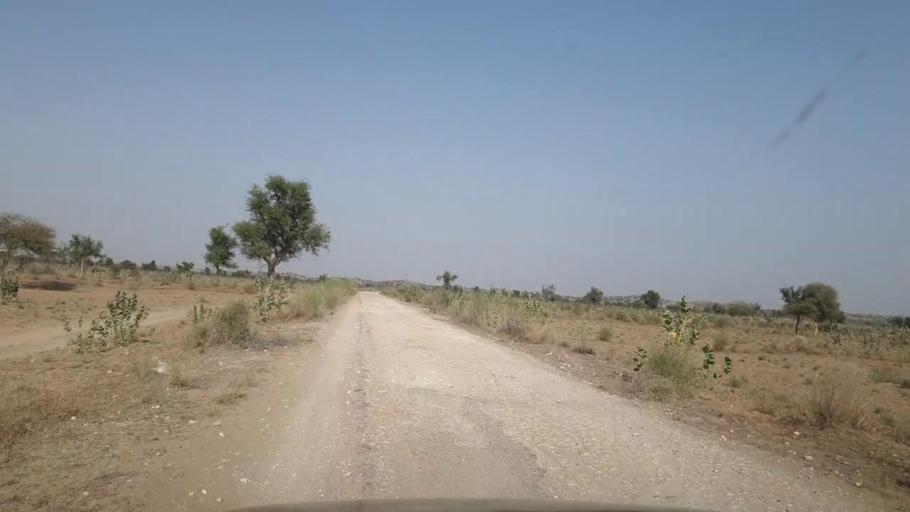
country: PK
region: Sindh
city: Islamkot
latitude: 25.0981
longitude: 70.4002
